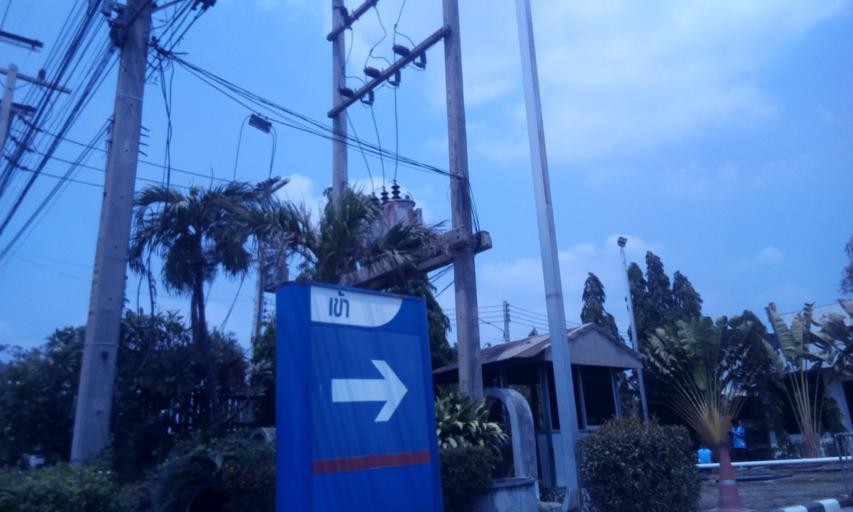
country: TH
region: Chachoengsao
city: Ban Pho
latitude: 13.6143
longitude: 101.1124
